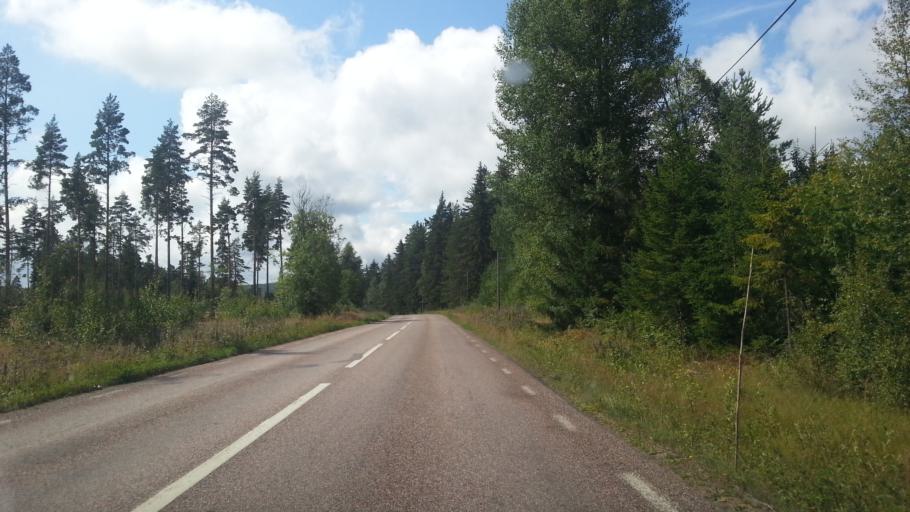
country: SE
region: Dalarna
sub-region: Faluns Kommun
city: Falun
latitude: 60.6424
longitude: 15.7826
